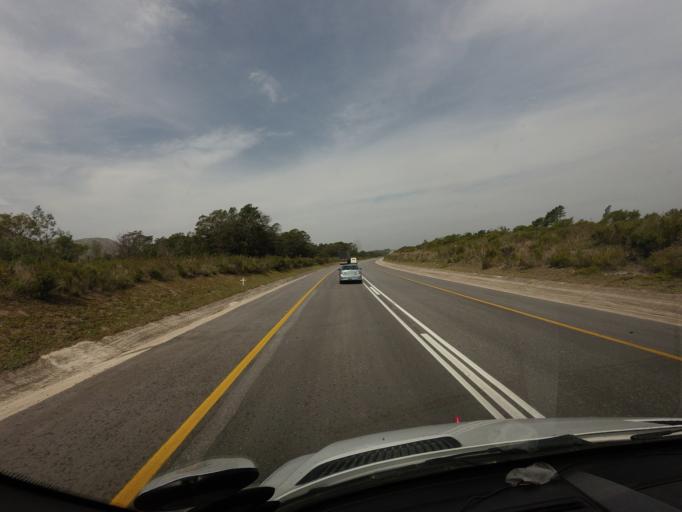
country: ZA
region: Eastern Cape
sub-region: Cacadu District Municipality
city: Kruisfontein
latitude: -33.9940
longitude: 24.7341
